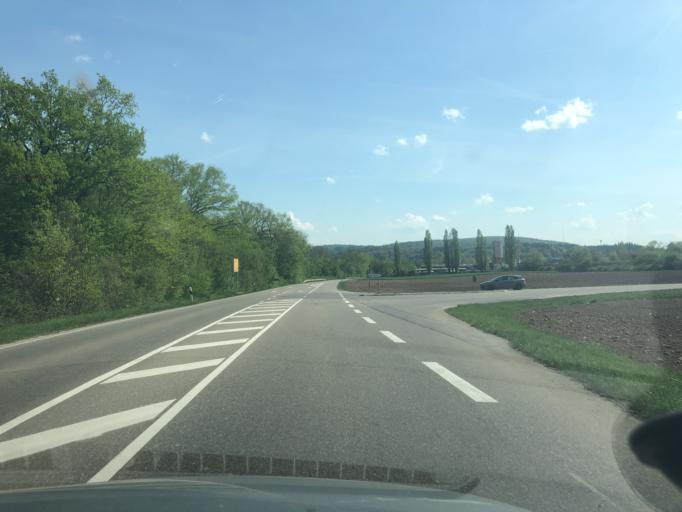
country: CH
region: Aargau
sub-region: Bezirk Zurzach
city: Koblenz
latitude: 47.6279
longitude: 8.2552
